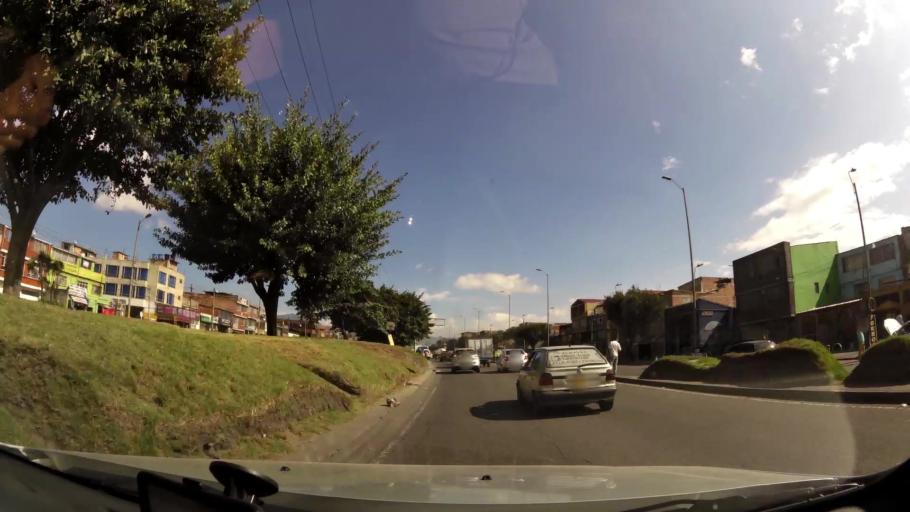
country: CO
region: Bogota D.C.
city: Bogota
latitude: 4.5893
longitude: -74.1453
